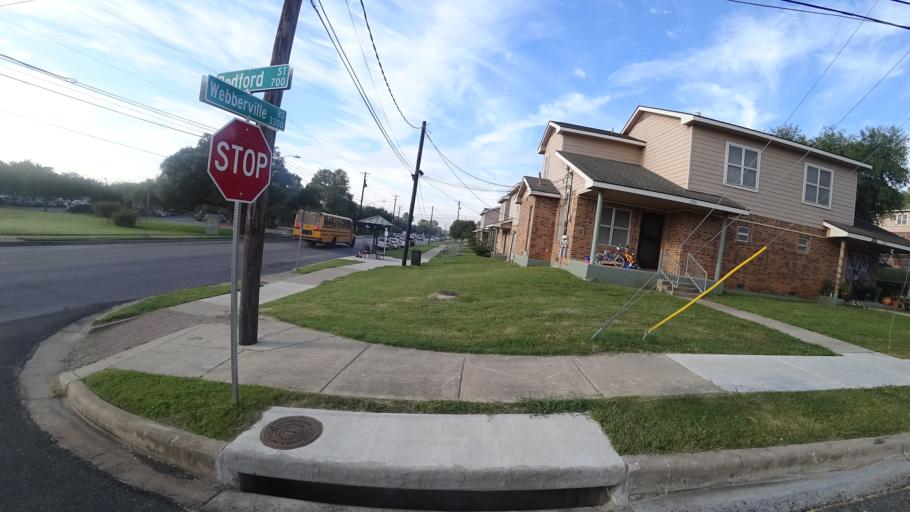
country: US
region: Texas
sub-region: Travis County
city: Austin
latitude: 30.2699
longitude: -97.7065
